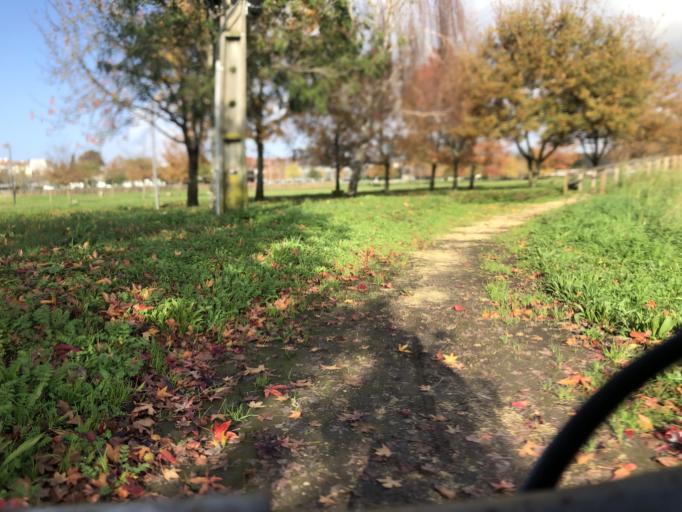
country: PT
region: Aveiro
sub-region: Estarreja
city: Estarreja
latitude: 40.7515
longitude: -8.5662
